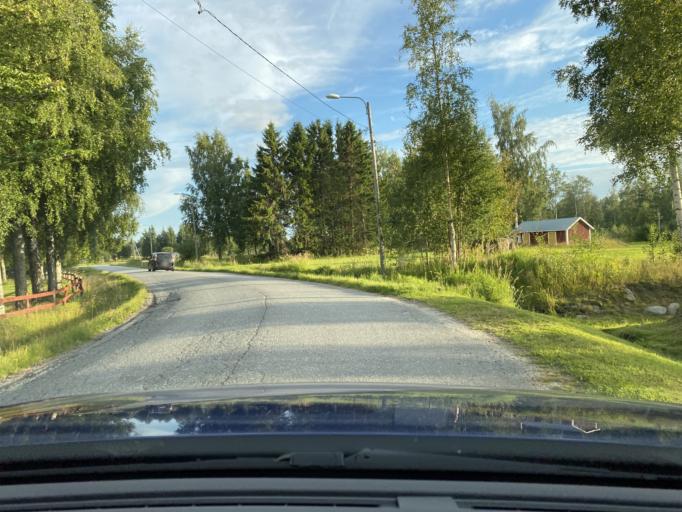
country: FI
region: Ostrobothnia
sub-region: Vaasa
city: Korsnaes
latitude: 62.9667
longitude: 21.1913
